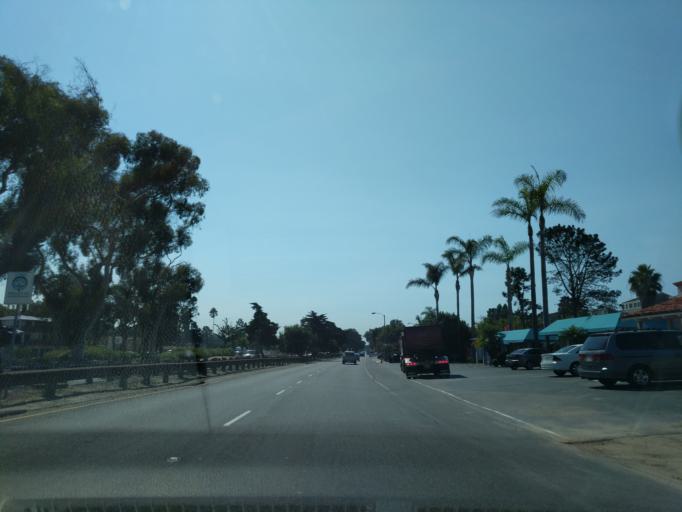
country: US
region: California
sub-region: San Diego County
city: Encinitas
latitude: 33.0811
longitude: -117.3080
